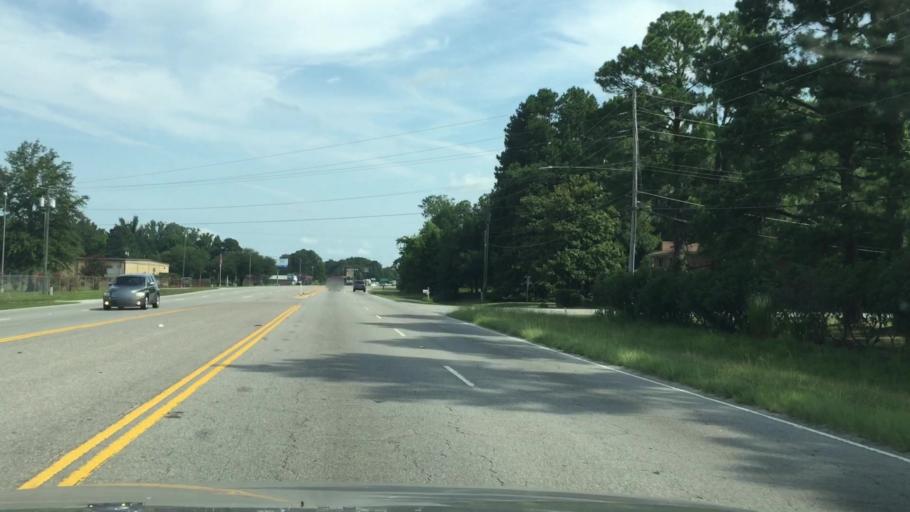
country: US
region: South Carolina
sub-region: Sumter County
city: South Sumter
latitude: 33.8980
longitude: -80.3530
